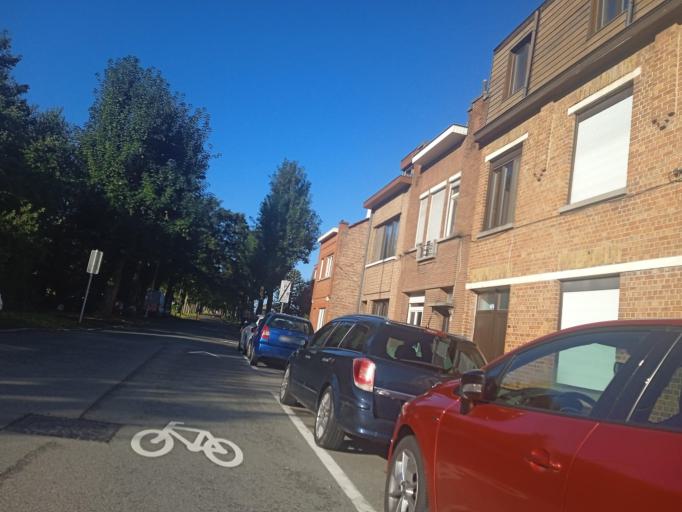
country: BE
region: Flanders
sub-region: Provincie Vlaams-Brabant
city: Dilbeek
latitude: 50.8346
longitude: 4.2785
